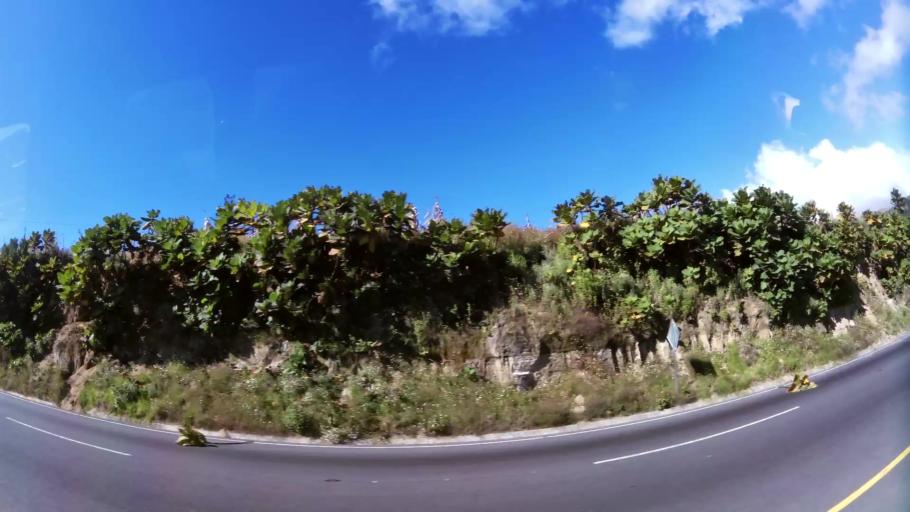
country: GT
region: Solola
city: Nahuala
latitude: 14.8210
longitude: -91.3345
